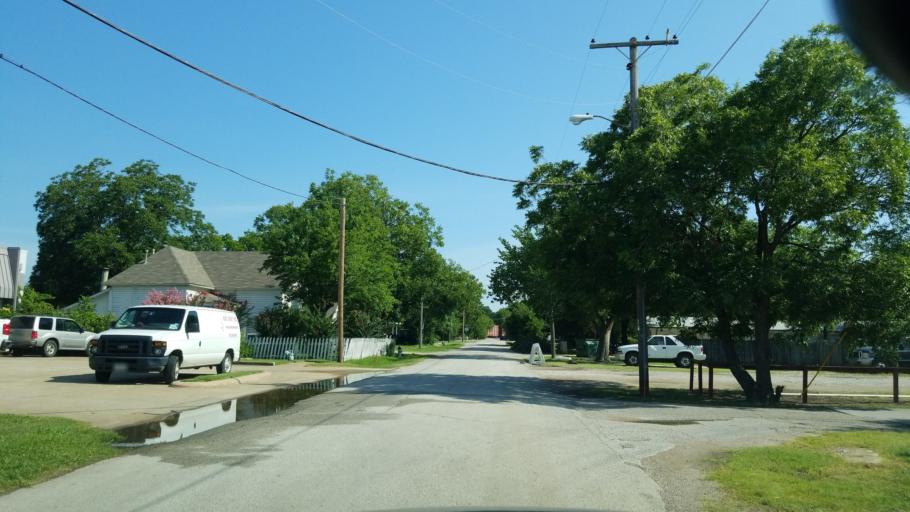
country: US
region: Texas
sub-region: Dallas County
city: Carrollton
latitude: 32.9542
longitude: -96.9058
